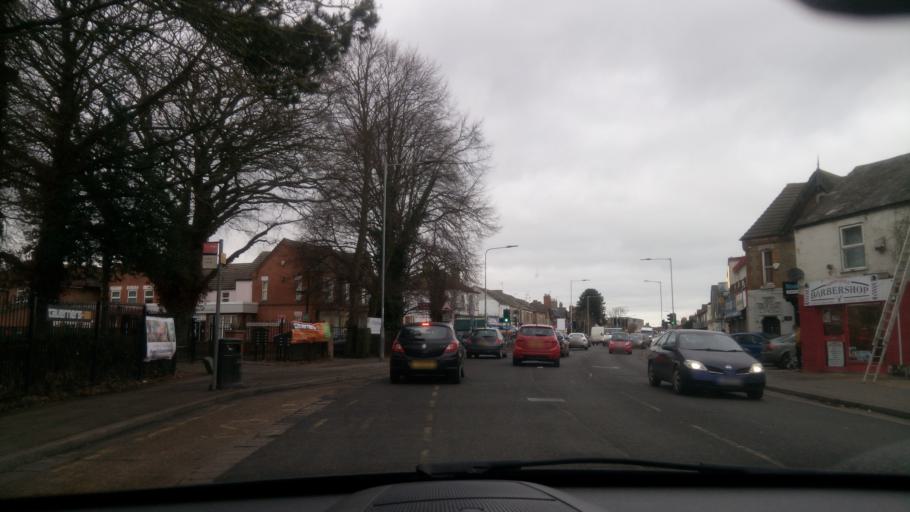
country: GB
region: England
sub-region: Peterborough
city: Peterborough
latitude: 52.5834
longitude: -0.2451
